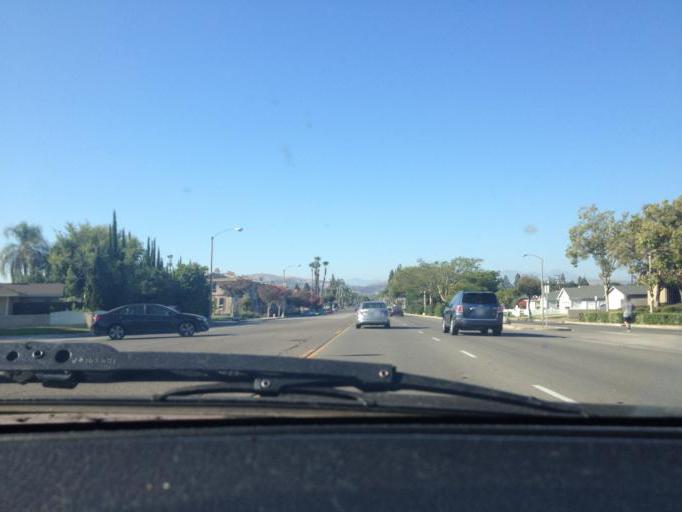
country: US
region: California
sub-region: Orange County
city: Brea
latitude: 33.9042
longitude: -117.9069
